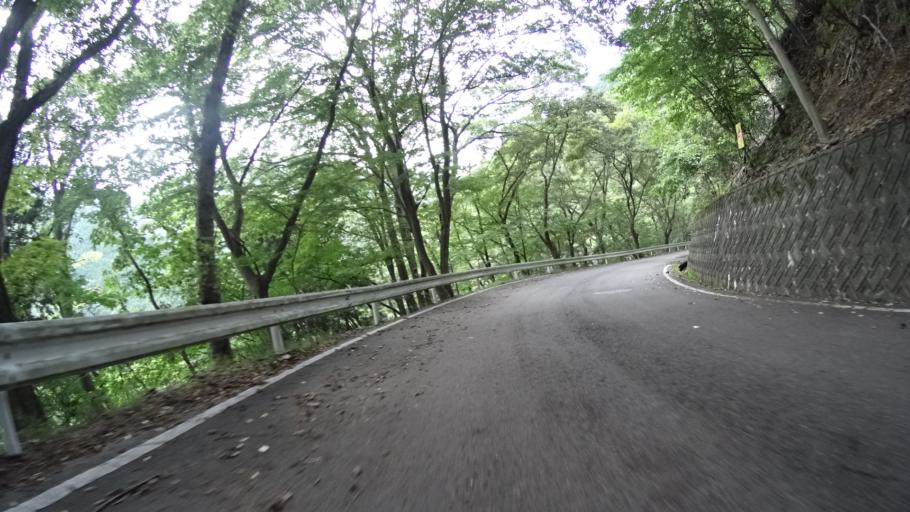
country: JP
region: Yamanashi
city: Enzan
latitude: 35.6062
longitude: 138.7962
